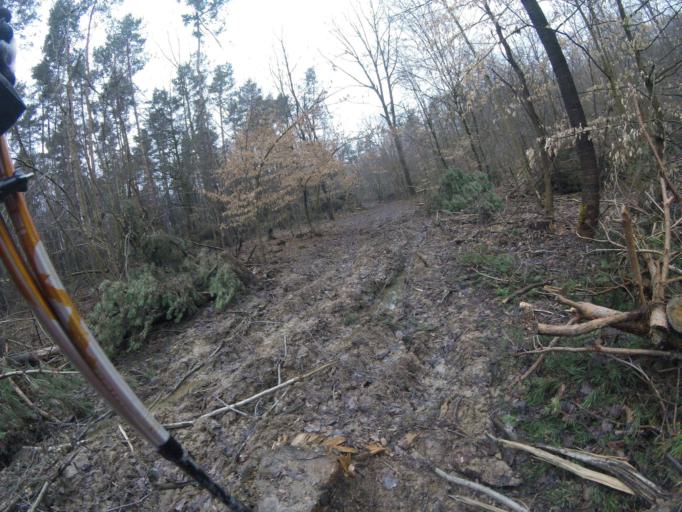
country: HU
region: Borsod-Abauj-Zemplen
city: Rudabanya
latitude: 48.4532
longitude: 20.5712
